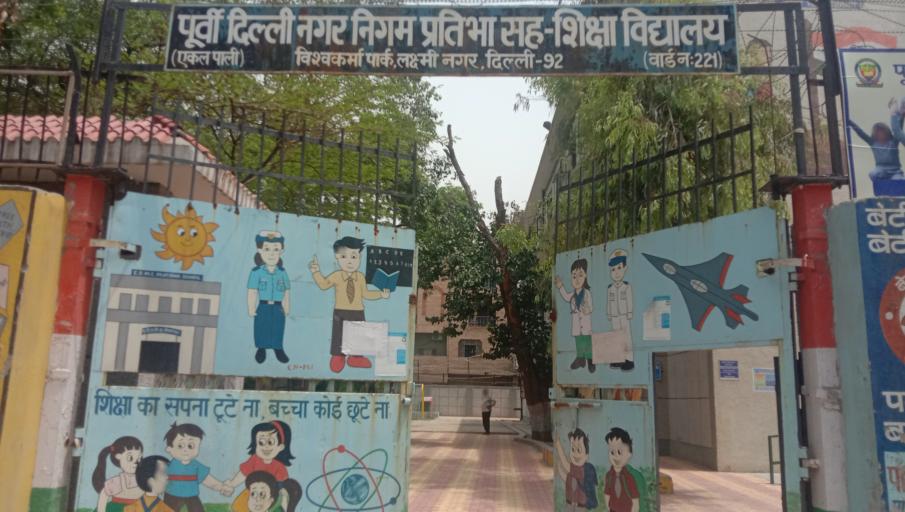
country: IN
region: NCT
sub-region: North Delhi
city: Delhi
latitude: 28.6389
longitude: 77.2717
